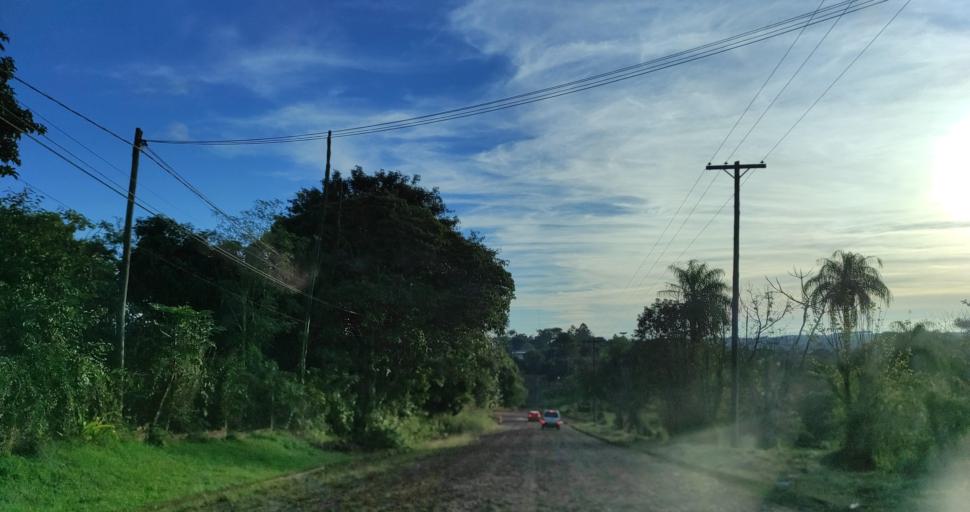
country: AR
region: Misiones
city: Puerto Rico
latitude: -26.7958
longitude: -55.0183
